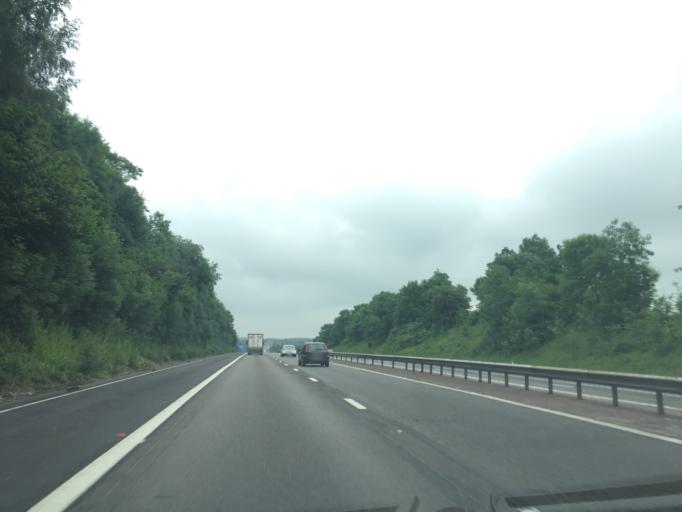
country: GB
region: England
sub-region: Hampshire
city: Overton
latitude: 51.2010
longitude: -1.1909
